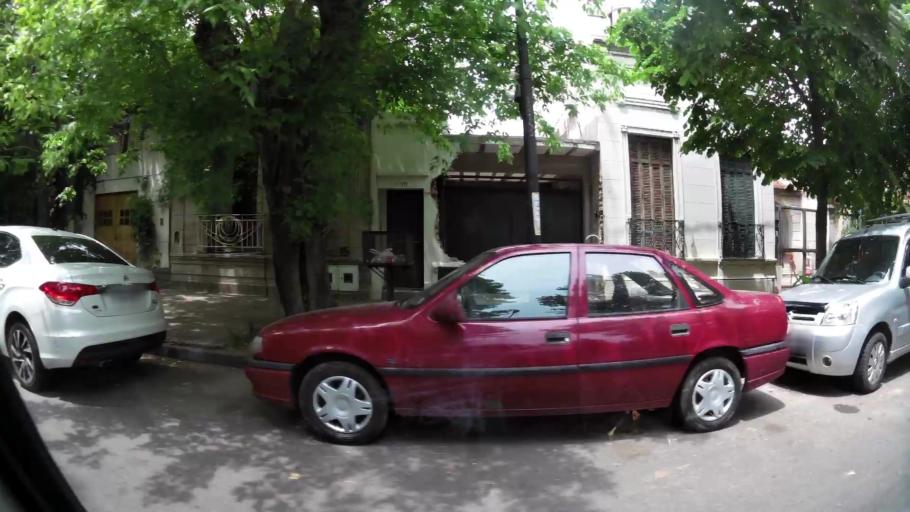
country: AR
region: Buenos Aires
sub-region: Partido de La Plata
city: La Plata
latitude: -34.9269
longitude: -57.9595
